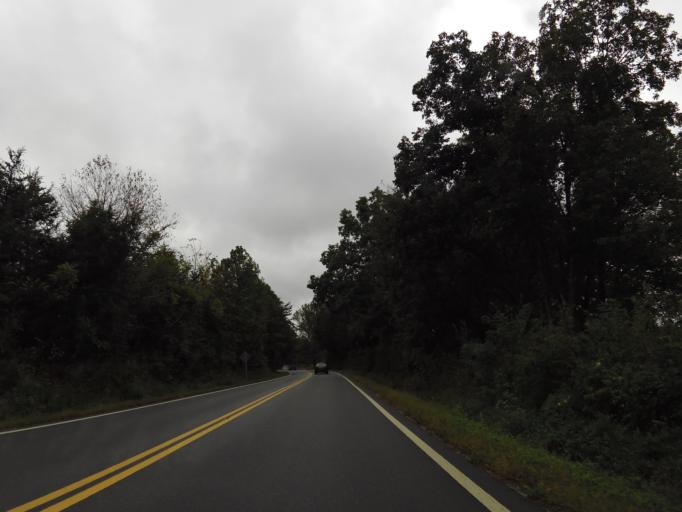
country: US
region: Tennessee
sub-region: Hamilton County
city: Lakesite
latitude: 35.1706
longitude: -85.0185
